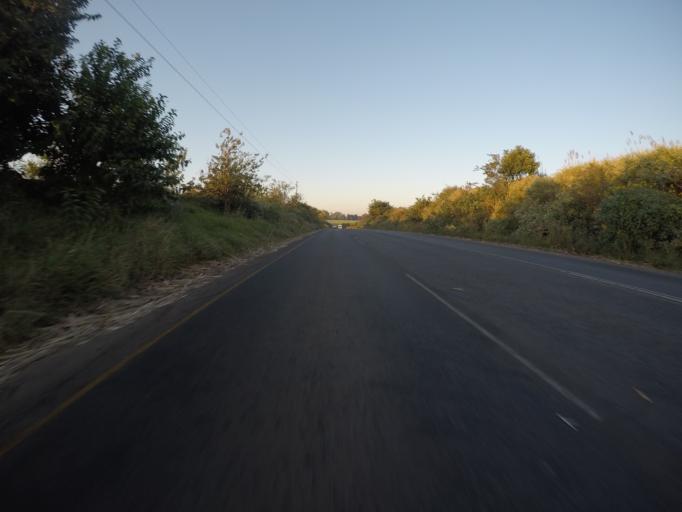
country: ZA
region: KwaZulu-Natal
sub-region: uThungulu District Municipality
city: Empangeni
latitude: -28.7908
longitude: 31.8972
